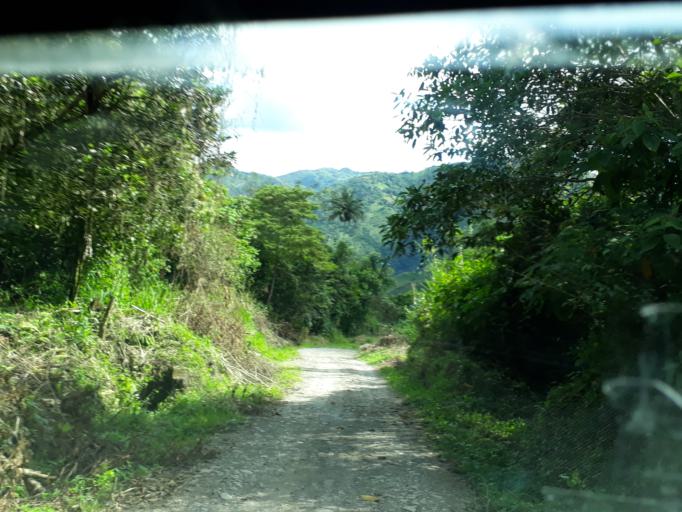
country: CO
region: Cundinamarca
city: Topaipi
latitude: 5.2783
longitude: -74.3524
